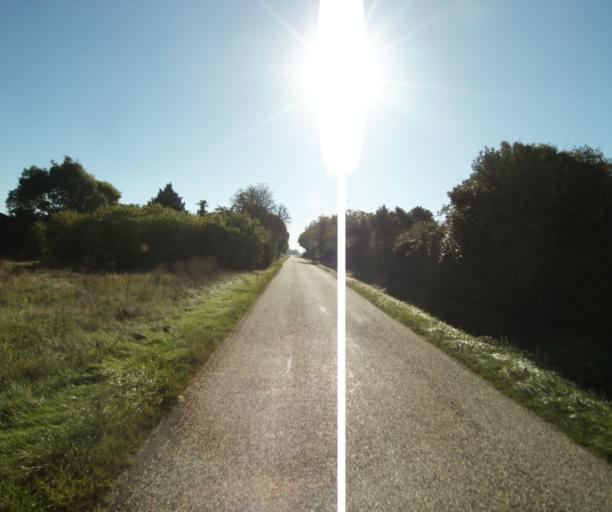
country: FR
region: Midi-Pyrenees
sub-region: Departement du Gers
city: Gondrin
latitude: 43.8258
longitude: 0.2684
